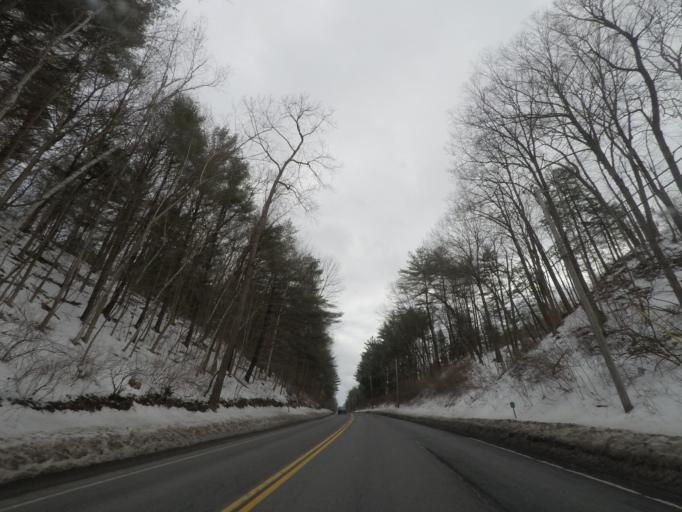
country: US
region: New York
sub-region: Saratoga County
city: Schuylerville
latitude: 43.0949
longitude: -73.5643
